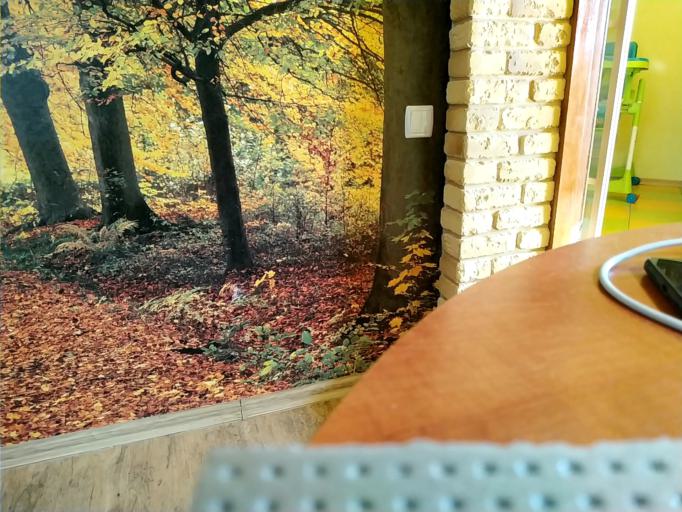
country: RU
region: Tverskaya
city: Kalashnikovo
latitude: 57.3457
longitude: 35.2260
